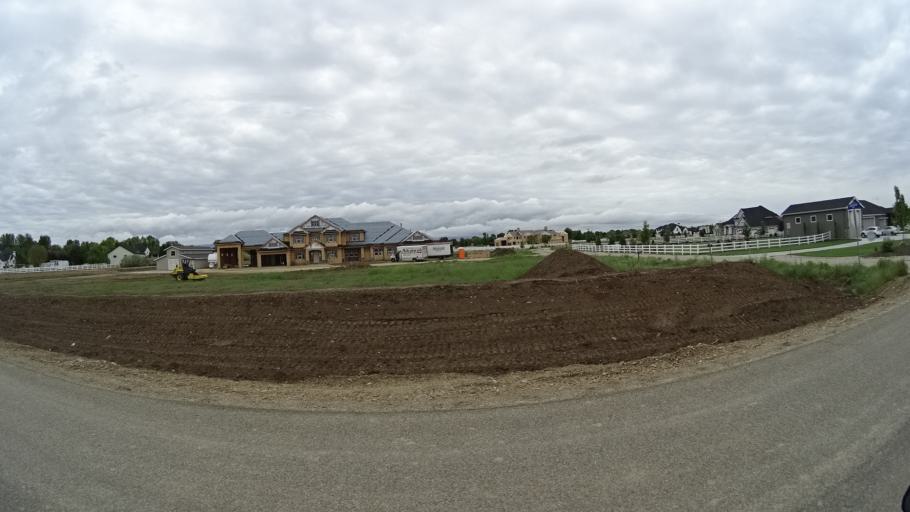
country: US
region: Idaho
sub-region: Ada County
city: Eagle
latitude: 43.7272
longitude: -116.4135
